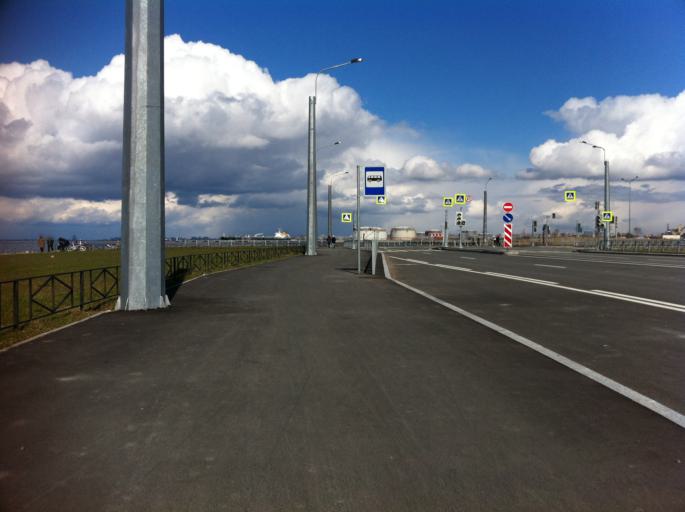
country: RU
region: St.-Petersburg
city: Sosnovaya Polyana
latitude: 59.8707
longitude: 30.1558
